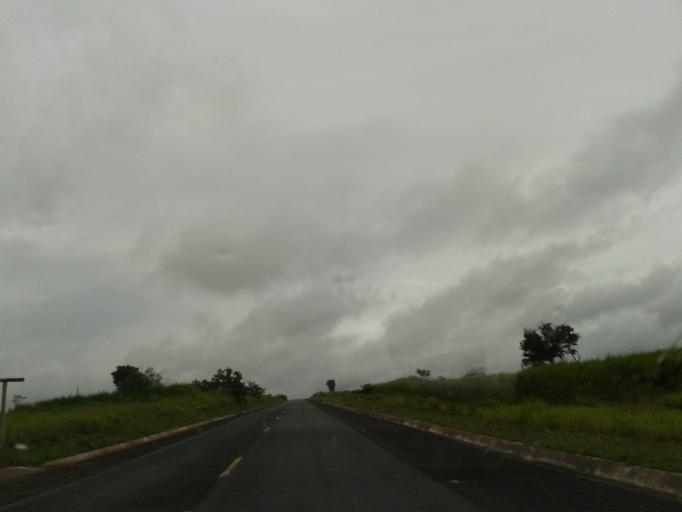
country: BR
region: Minas Gerais
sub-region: Santa Vitoria
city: Santa Vitoria
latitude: -19.2629
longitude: -50.0077
